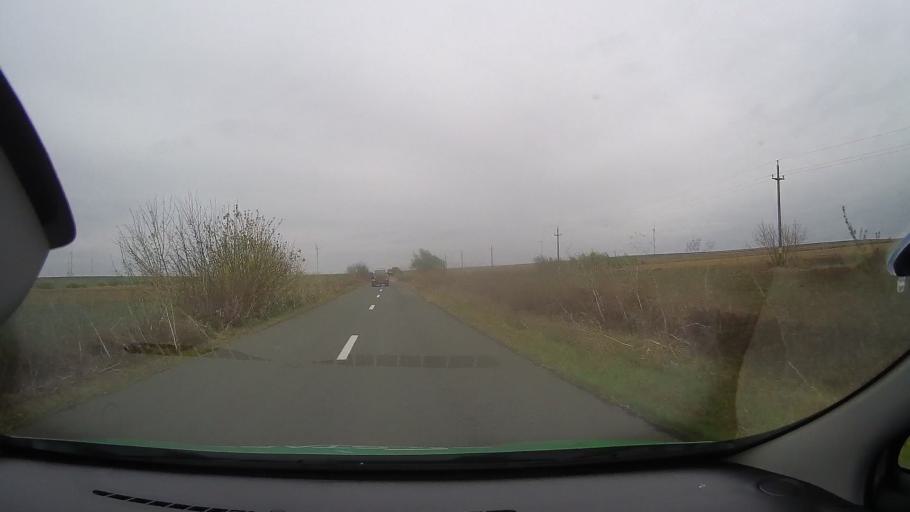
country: RO
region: Constanta
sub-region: Comuna Targusor
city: Targusor
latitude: 44.4690
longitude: 28.3902
